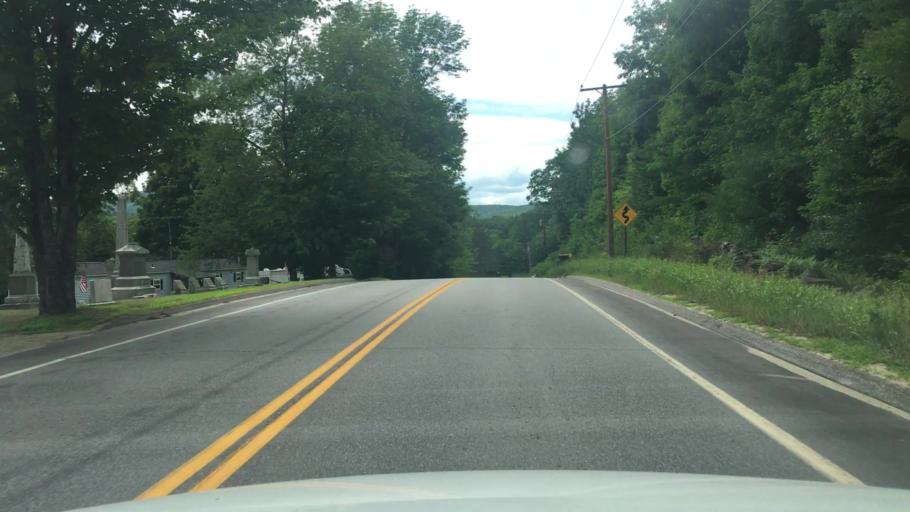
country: US
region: Maine
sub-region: Oxford County
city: Paris
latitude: 44.3688
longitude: -70.4641
